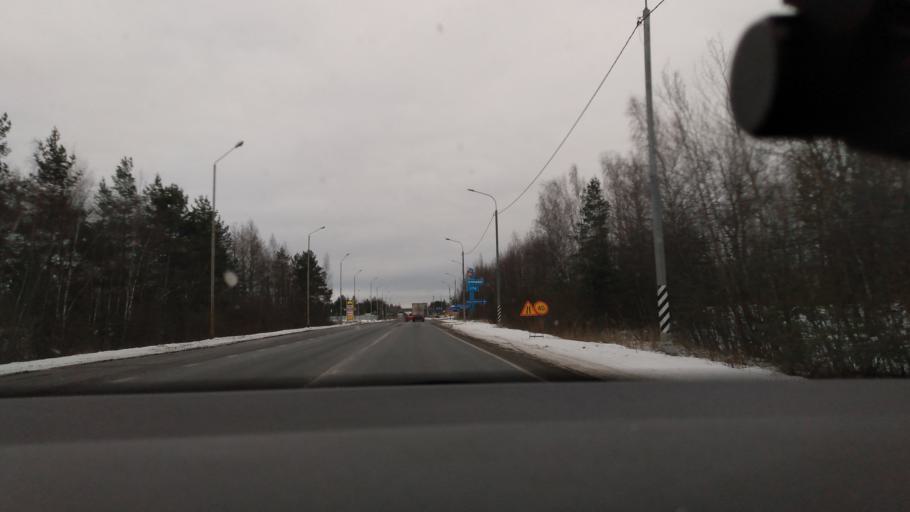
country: RU
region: Moskovskaya
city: Yegor'yevsk
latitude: 55.4197
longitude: 39.0413
